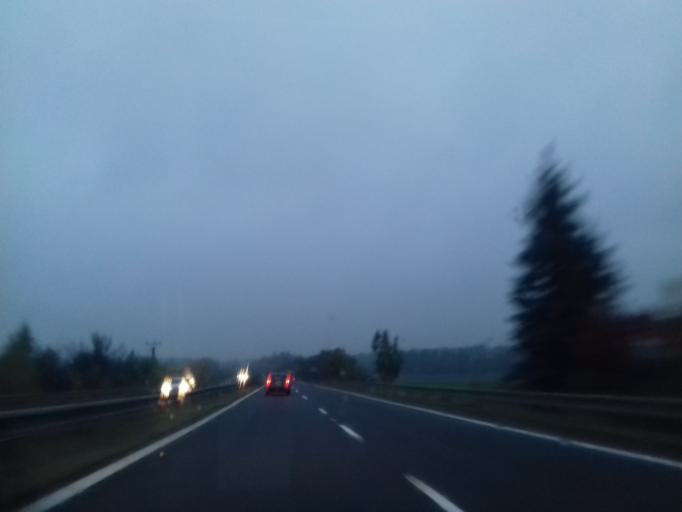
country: CZ
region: Olomoucky
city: Litovel
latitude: 49.6960
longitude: 17.0442
